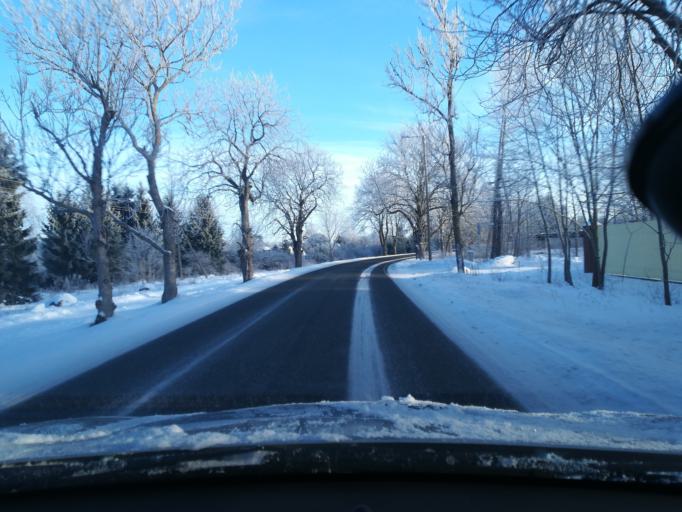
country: EE
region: Harju
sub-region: Keila linn
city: Keila
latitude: 59.3971
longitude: 24.3128
